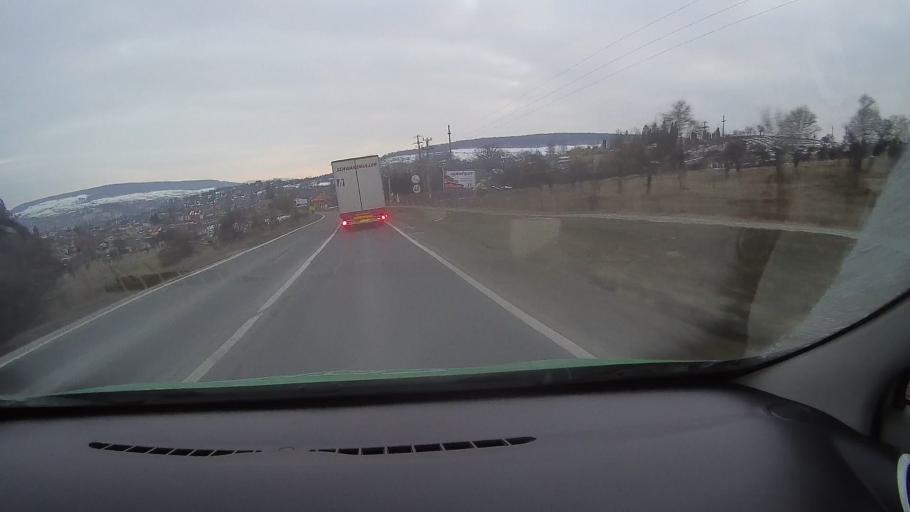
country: RO
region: Harghita
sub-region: Municipiul Odorheiu Secuiesc
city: Odorheiu Secuiesc
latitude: 46.3211
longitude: 25.2800
